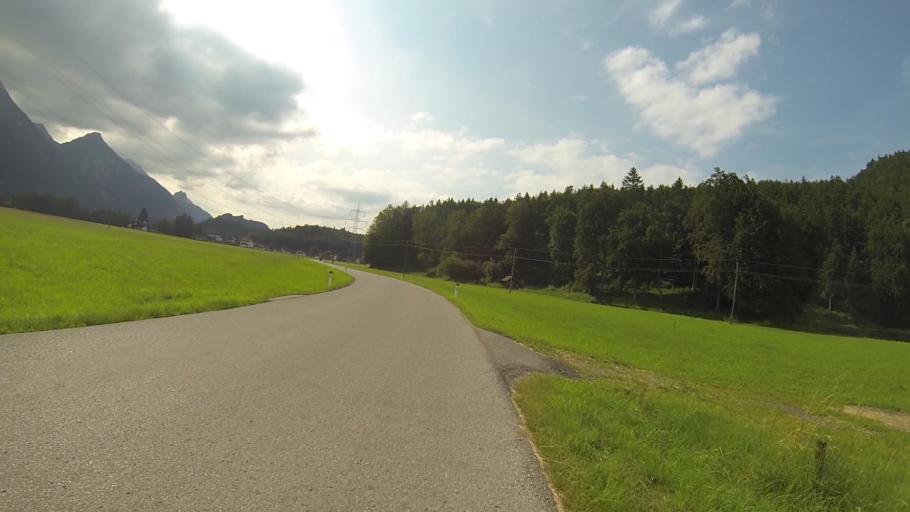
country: AT
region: Tyrol
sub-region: Politischer Bezirk Reutte
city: Pflach
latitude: 47.5341
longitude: 10.6958
